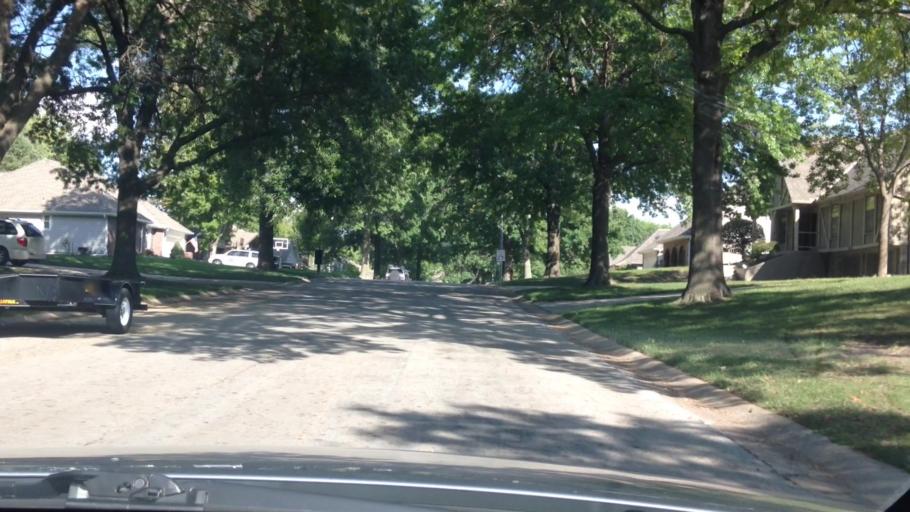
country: US
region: Kansas
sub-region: Johnson County
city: Leawood
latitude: 38.8979
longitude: -94.6126
